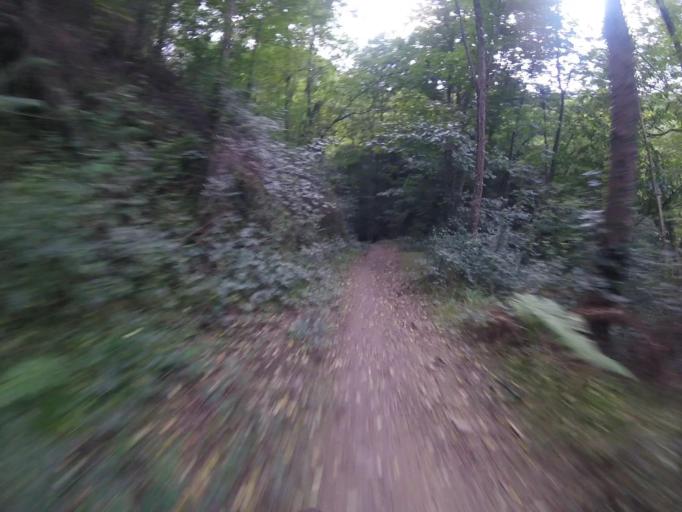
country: ES
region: Basque Country
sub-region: Provincia de Guipuzcoa
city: Errenteria
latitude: 43.2705
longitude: -1.8390
